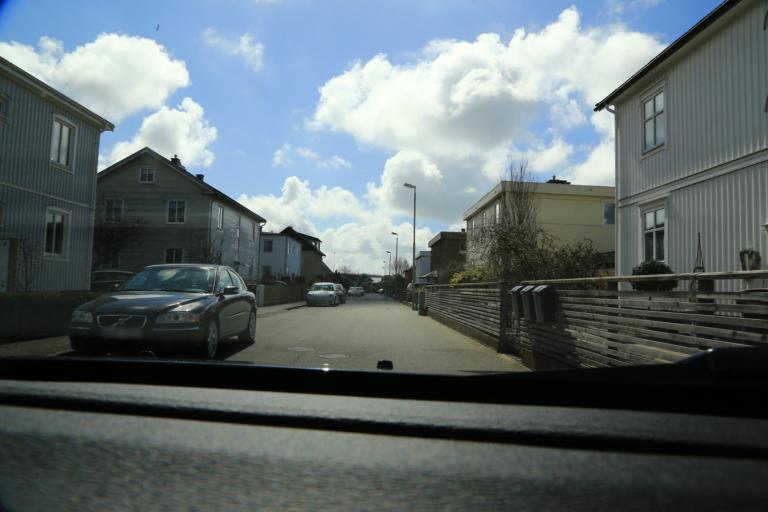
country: SE
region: Halland
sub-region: Varbergs Kommun
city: Varberg
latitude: 57.1084
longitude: 12.2685
